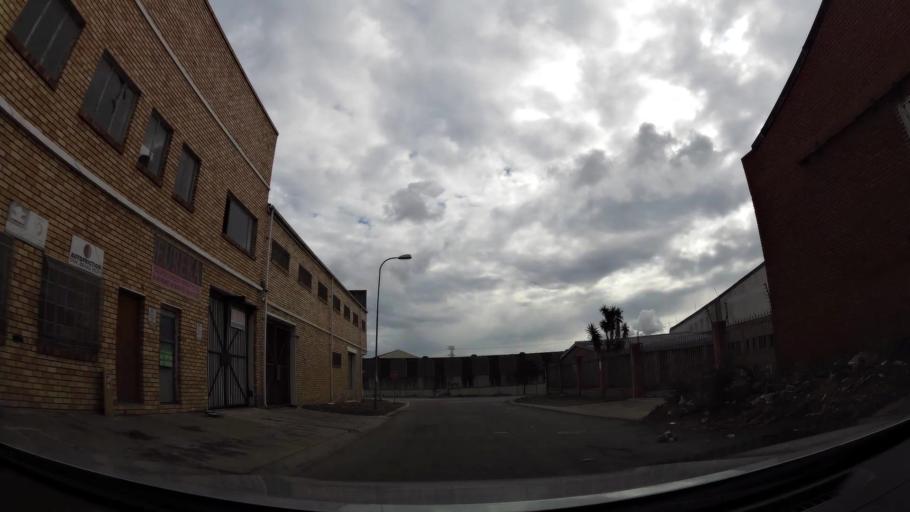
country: ZA
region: Eastern Cape
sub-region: Nelson Mandela Bay Metropolitan Municipality
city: Port Elizabeth
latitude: -33.9269
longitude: 25.5823
